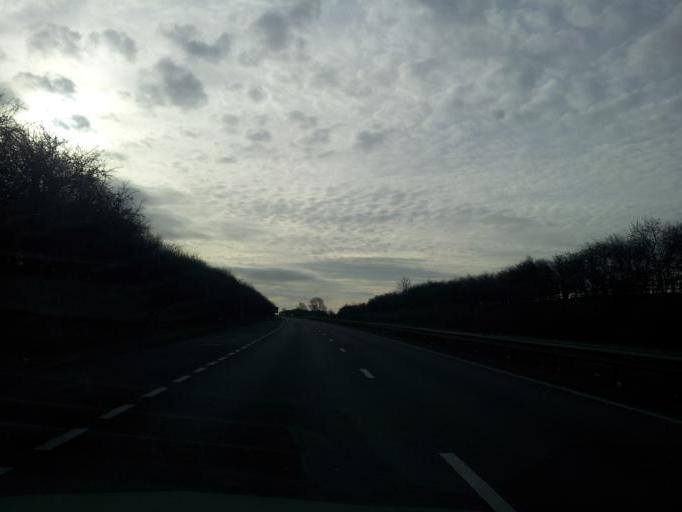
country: GB
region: England
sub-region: District of Rutland
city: Tinwell
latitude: 52.6635
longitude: -0.5220
